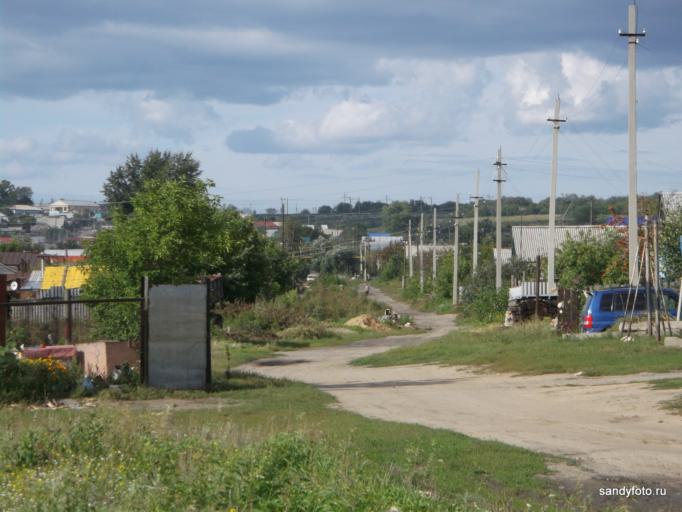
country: RU
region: Chelyabinsk
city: Troitsk
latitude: 54.0874
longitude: 61.5918
